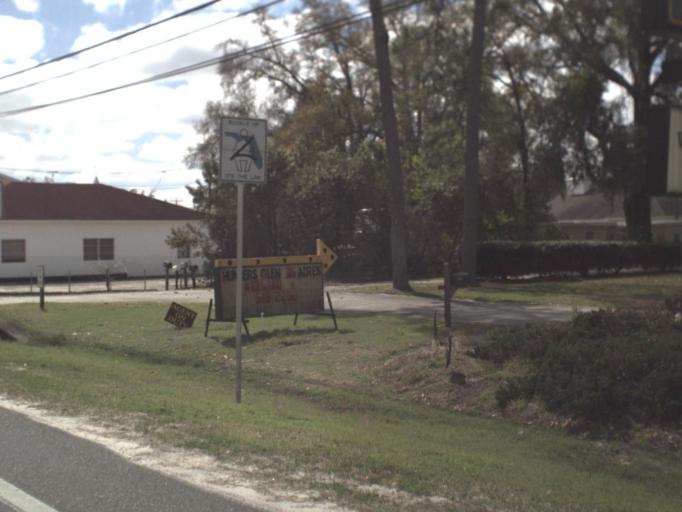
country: US
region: Florida
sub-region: Wakulla County
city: Crawfordville
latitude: 30.1780
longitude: -84.3751
